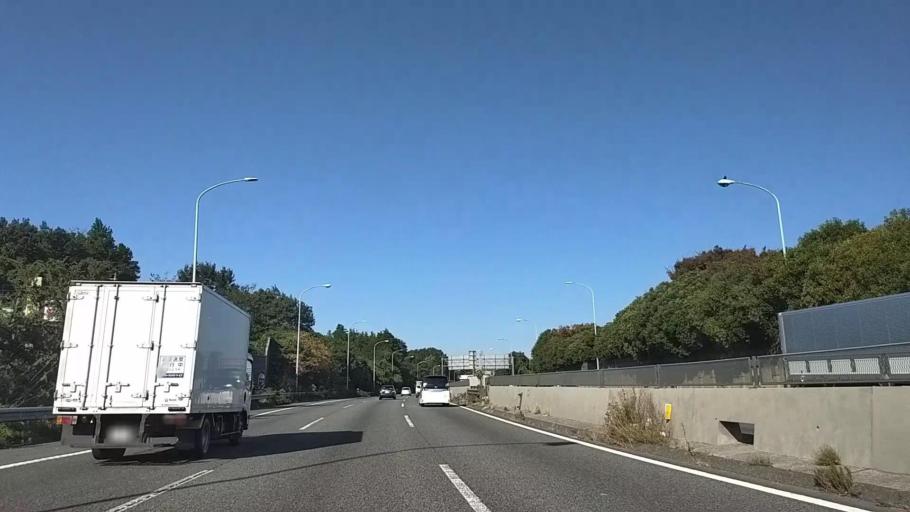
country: JP
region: Kanagawa
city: Yokohama
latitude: 35.4545
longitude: 139.5530
